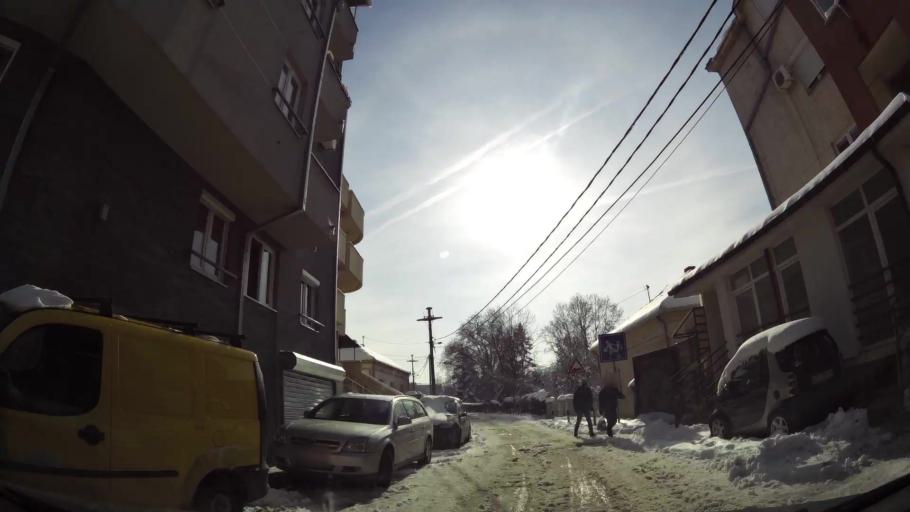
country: RS
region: Central Serbia
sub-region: Belgrade
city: Palilula
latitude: 44.7981
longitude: 20.5290
